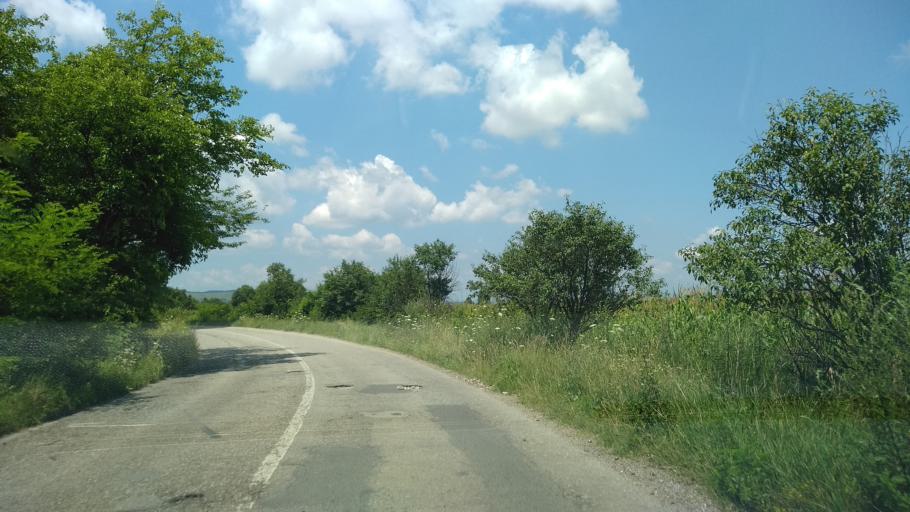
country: RO
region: Hunedoara
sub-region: Comuna Bretea Romana
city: Bretea Romana
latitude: 45.7016
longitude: 23.0170
